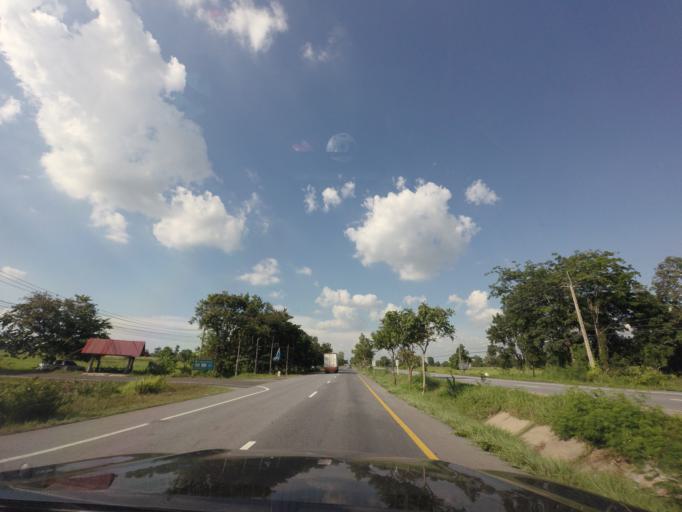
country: TH
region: Khon Kaen
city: Phon
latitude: 15.7143
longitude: 102.5891
